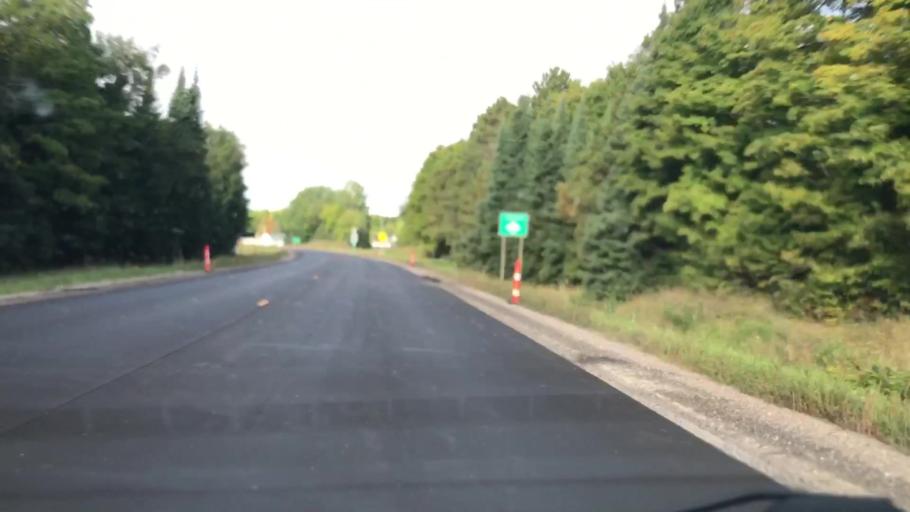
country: US
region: Michigan
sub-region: Luce County
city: Newberry
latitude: 46.3464
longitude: -85.0246
